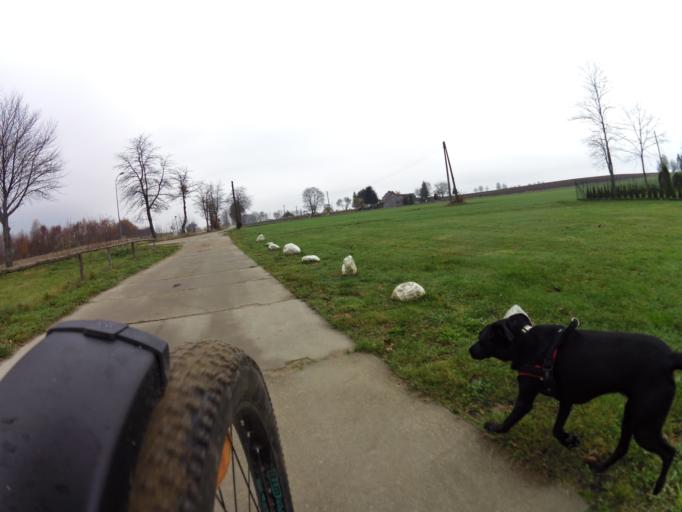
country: PL
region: Pomeranian Voivodeship
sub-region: Powiat pucki
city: Krokowa
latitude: 54.7172
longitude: 18.1386
